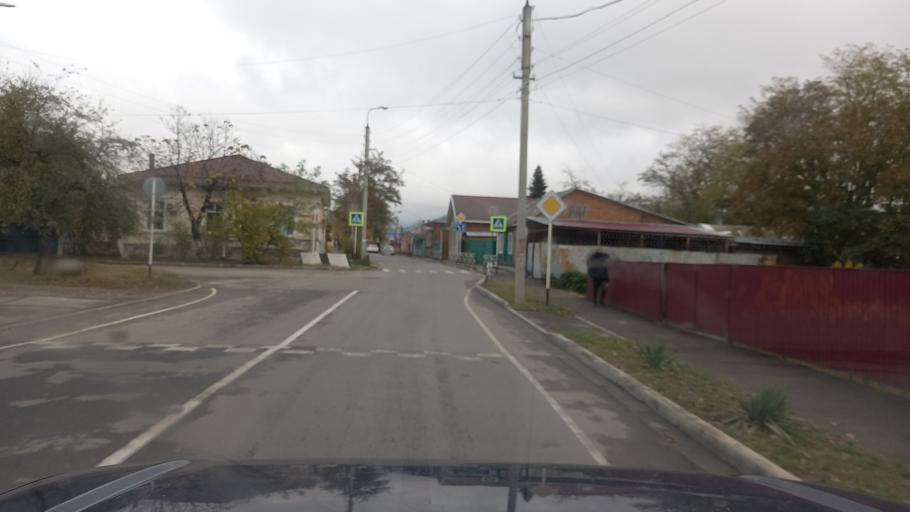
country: RU
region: Adygeya
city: Maykop
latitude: 44.6022
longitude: 40.0892
